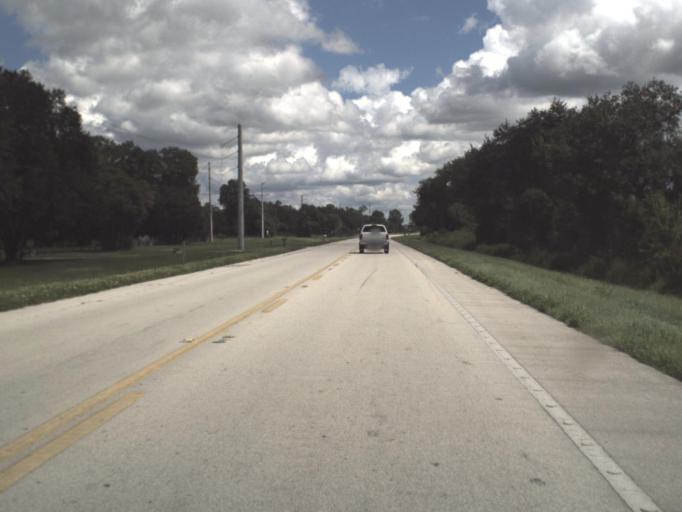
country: US
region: Florida
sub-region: DeSoto County
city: Southeast Arcadia
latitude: 27.2089
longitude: -81.8033
